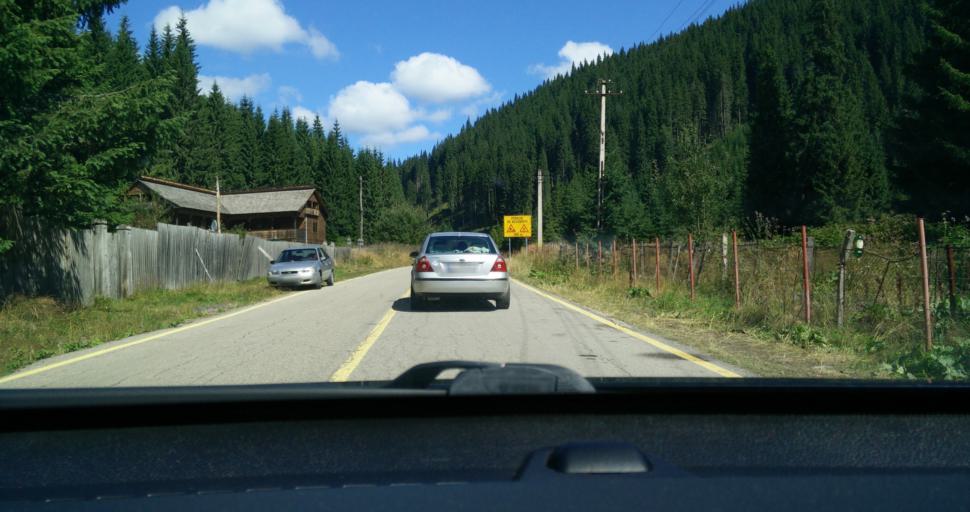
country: RO
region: Hunedoara
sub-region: Oras Petrila
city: Petrila
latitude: 45.4360
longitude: 23.6300
